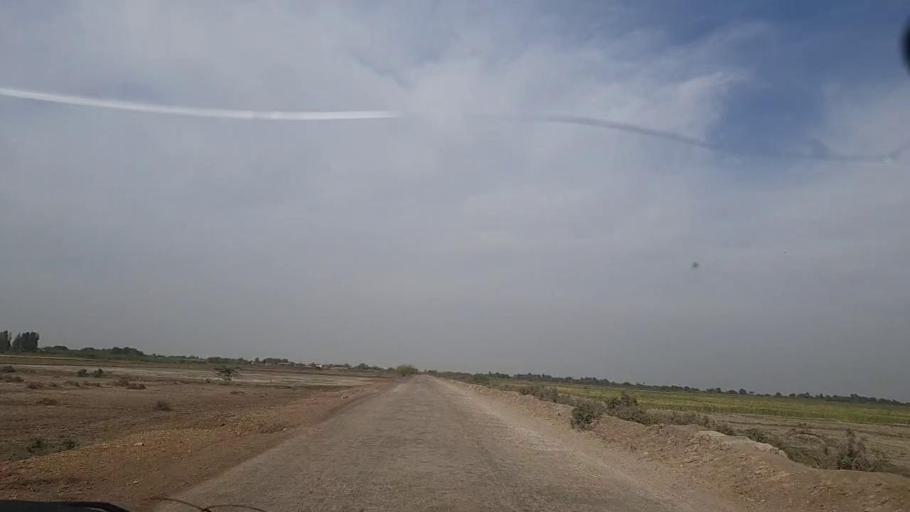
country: PK
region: Sindh
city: Pithoro
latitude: 25.5351
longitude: 69.3606
